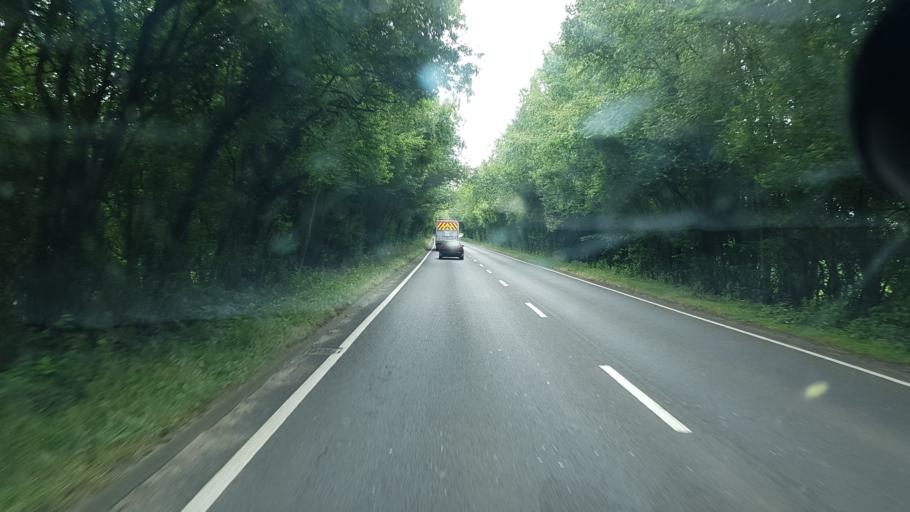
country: GB
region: England
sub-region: Surrey
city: Godstone
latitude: 51.2455
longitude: -0.0503
